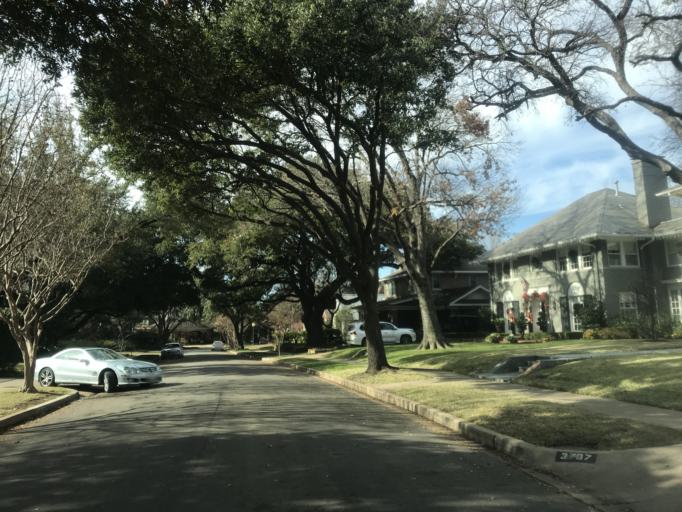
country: US
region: Texas
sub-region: Dallas County
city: Highland Park
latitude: 32.8221
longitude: -96.7959
